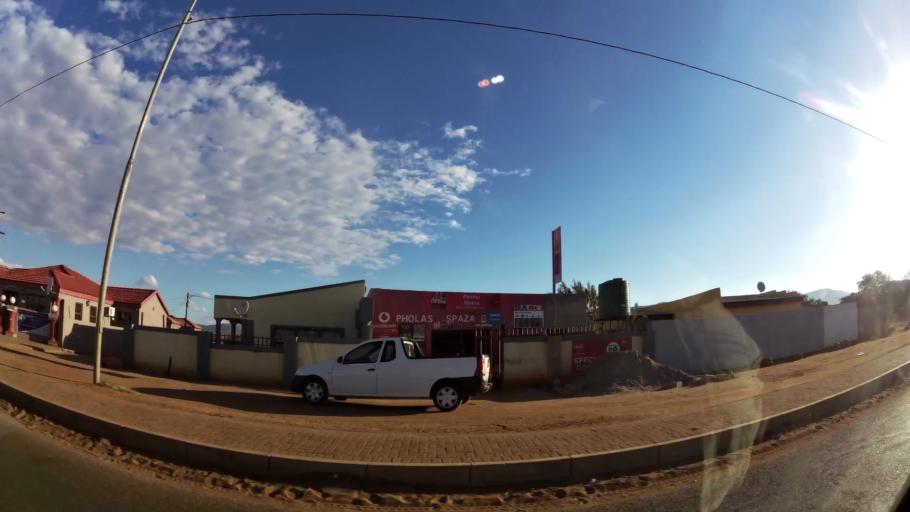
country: ZA
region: Limpopo
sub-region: Waterberg District Municipality
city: Mokopane
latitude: -24.1657
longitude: 28.9941
